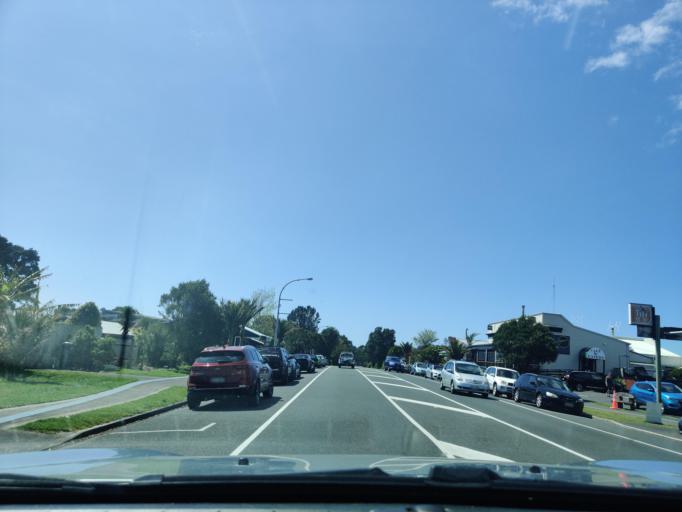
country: NZ
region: Taranaki
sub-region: New Plymouth District
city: New Plymouth
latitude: -39.1163
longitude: 173.9568
